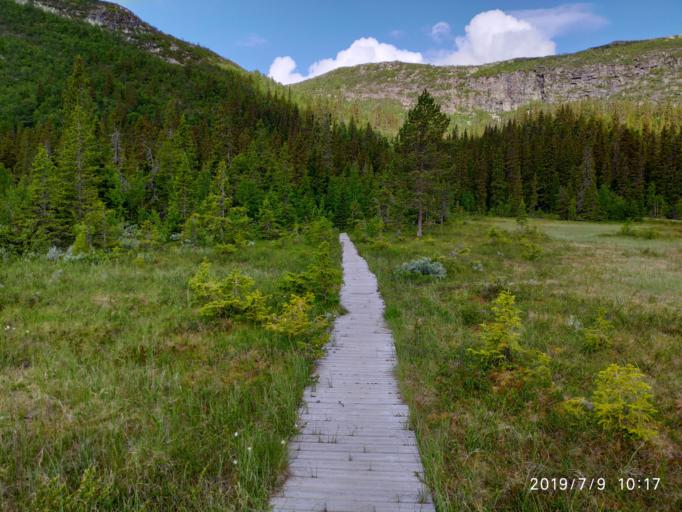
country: NO
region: Buskerud
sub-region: Nes
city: Nesbyen
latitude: 60.3399
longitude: 9.1781
